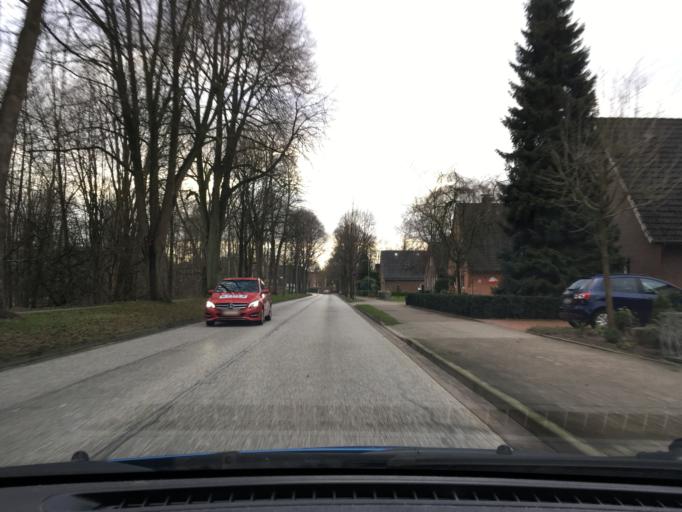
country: DE
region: Schleswig-Holstein
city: Ottenbuttel
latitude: 53.9485
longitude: 9.4943
